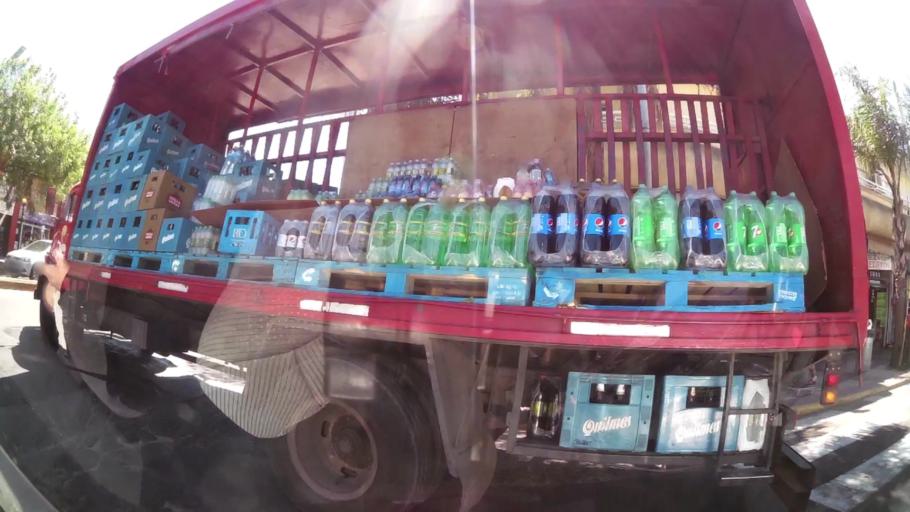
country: AR
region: Buenos Aires
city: Hurlingham
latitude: -34.5006
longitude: -58.6432
